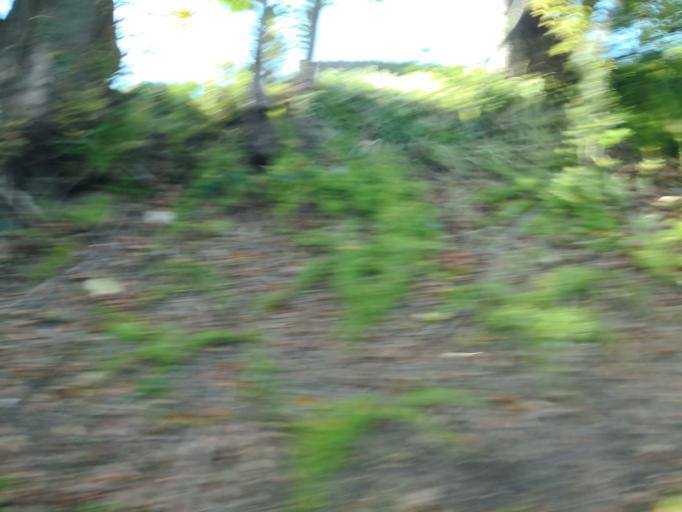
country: AU
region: New South Wales
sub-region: Gosford Shire
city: Gosford
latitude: -33.4137
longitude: 151.3446
